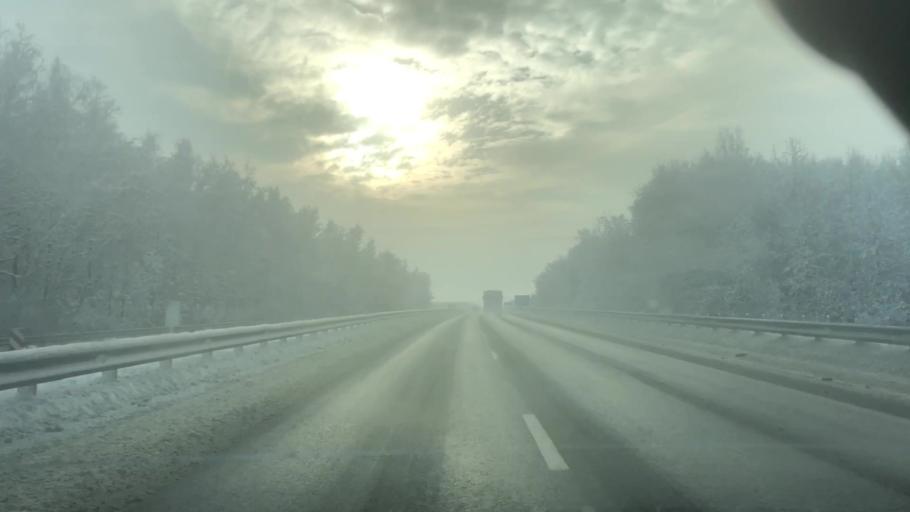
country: RU
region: Tula
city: Venev
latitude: 54.3814
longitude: 38.1550
